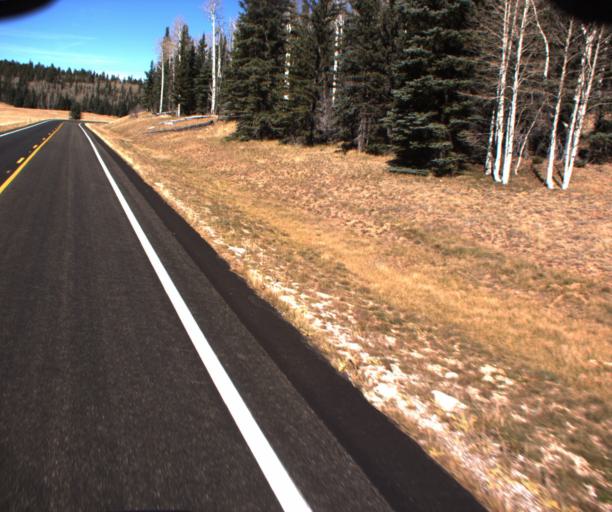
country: US
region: Arizona
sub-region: Coconino County
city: Grand Canyon
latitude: 36.4381
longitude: -112.1349
